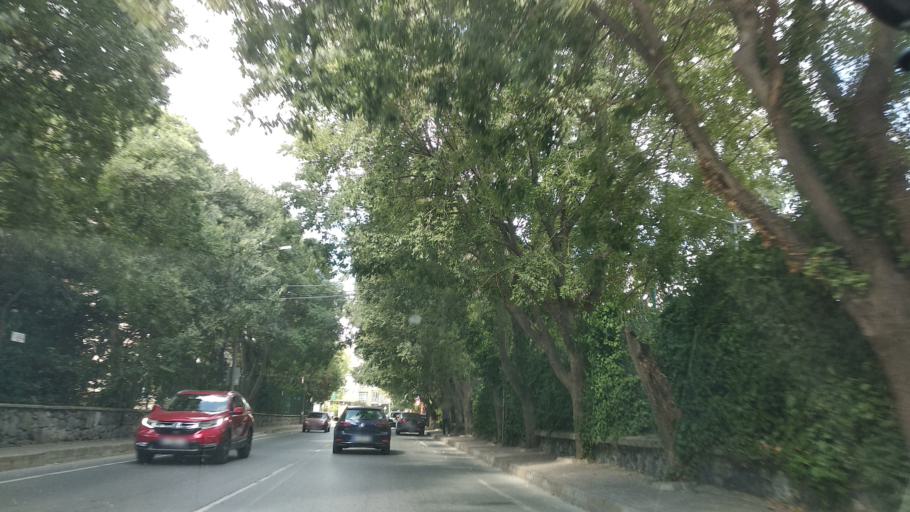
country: TR
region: Istanbul
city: Sisli
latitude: 41.0850
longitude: 29.0403
